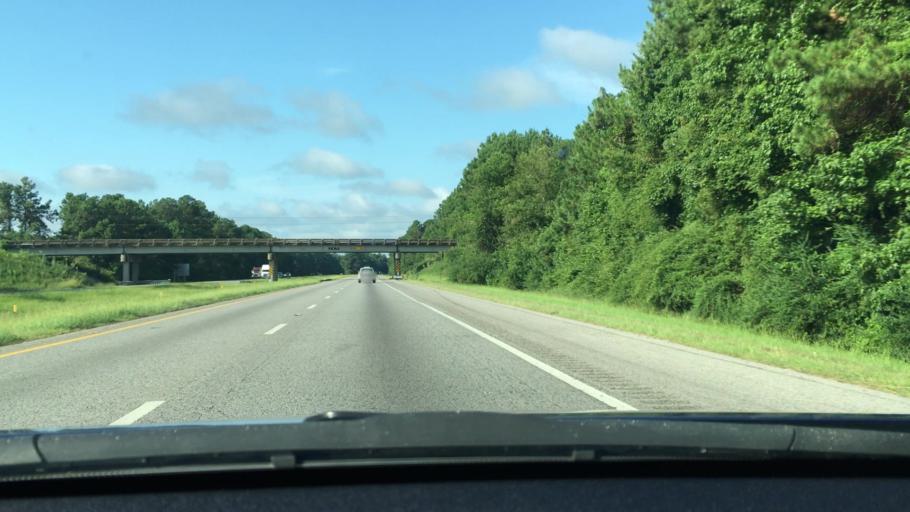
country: US
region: South Carolina
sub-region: Clarendon County
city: Manning
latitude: 33.6887
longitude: -80.2571
